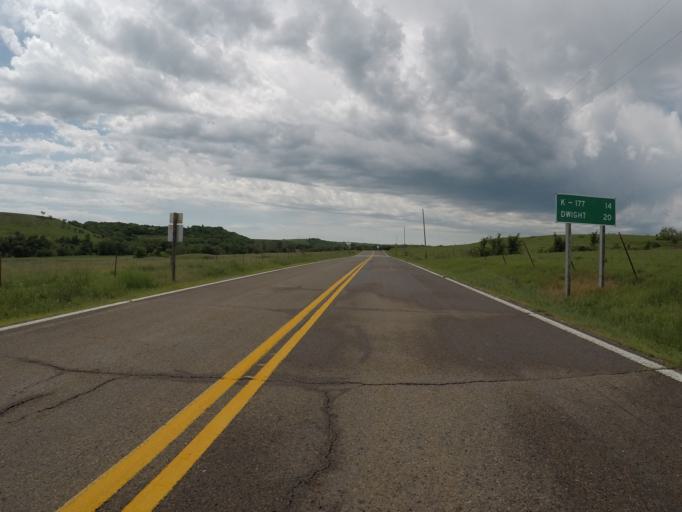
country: US
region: Kansas
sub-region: Wabaunsee County
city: Alma
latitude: 38.8891
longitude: -96.2814
